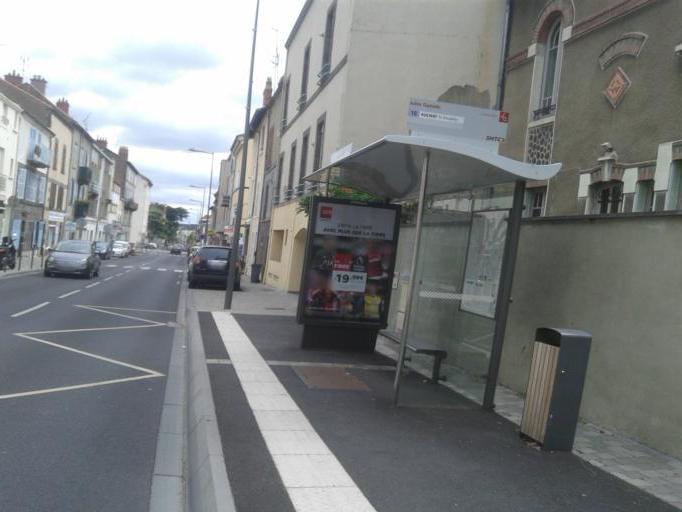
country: FR
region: Auvergne
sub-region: Departement du Puy-de-Dome
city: Chamalieres
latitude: 45.7776
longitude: 3.0643
